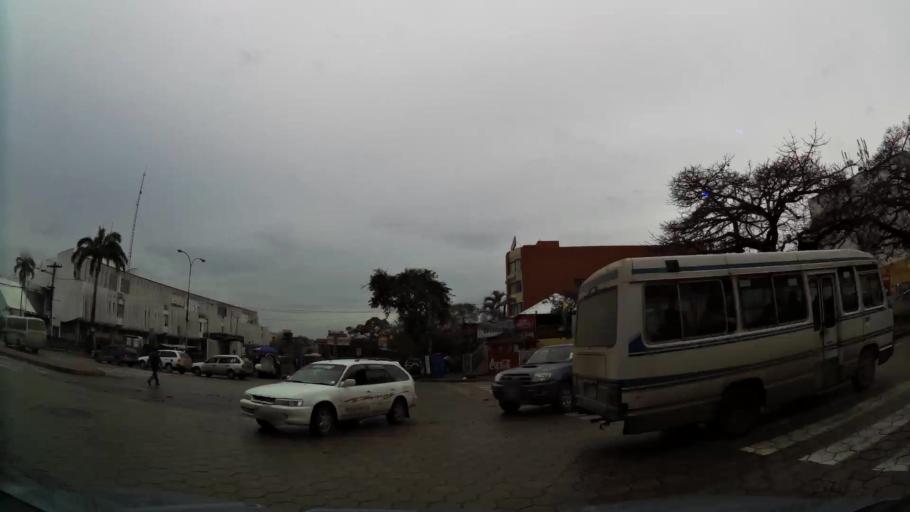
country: BO
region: Santa Cruz
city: Santa Cruz de la Sierra
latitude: -17.7932
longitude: -63.1858
